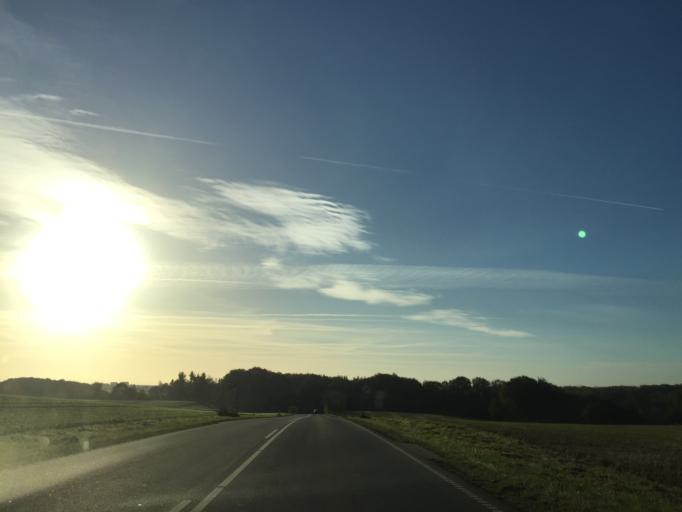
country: DK
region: Central Jutland
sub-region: Skanderborg Kommune
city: Skanderborg
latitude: 56.0638
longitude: 9.8999
